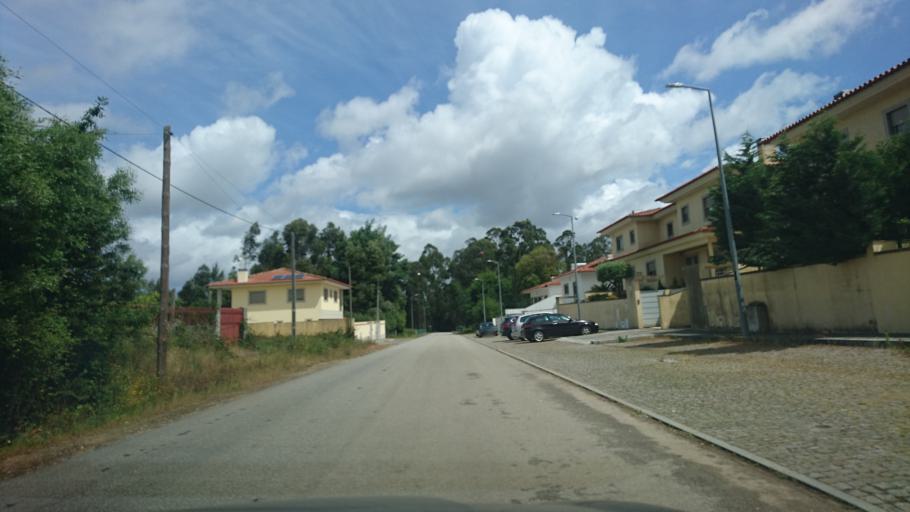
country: PT
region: Aveiro
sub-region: Santa Maria da Feira
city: Rio Meao
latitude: 40.9254
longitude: -8.5859
